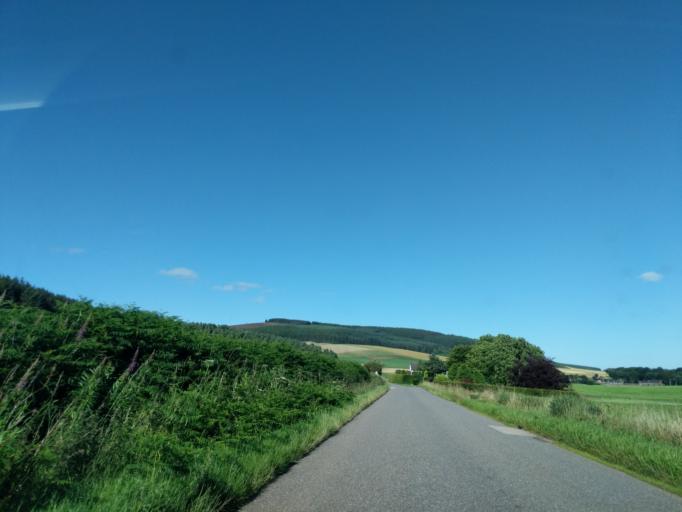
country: GB
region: Scotland
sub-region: Aberdeenshire
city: Laurencekirk
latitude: 56.8709
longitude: -2.5547
